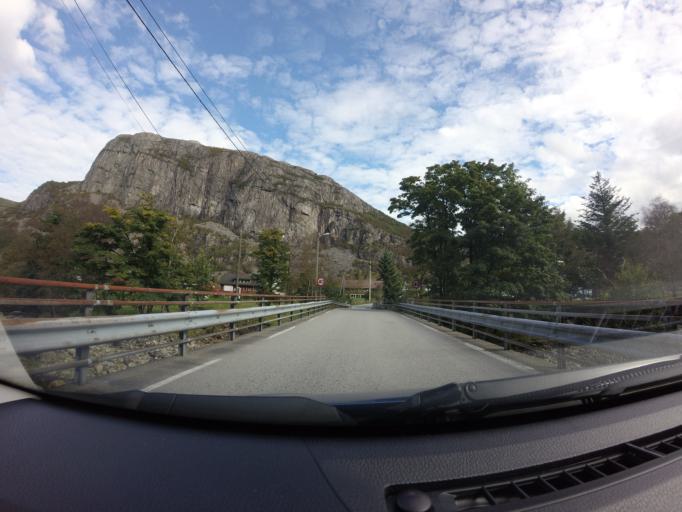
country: NO
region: Rogaland
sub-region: Forsand
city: Forsand
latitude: 58.8055
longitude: 6.2530
